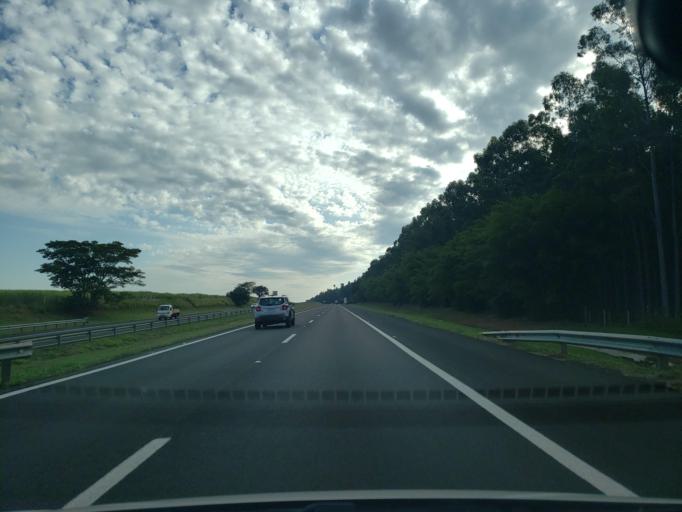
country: BR
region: Sao Paulo
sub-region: Guararapes
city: Guararapes
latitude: -21.2001
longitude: -50.5607
